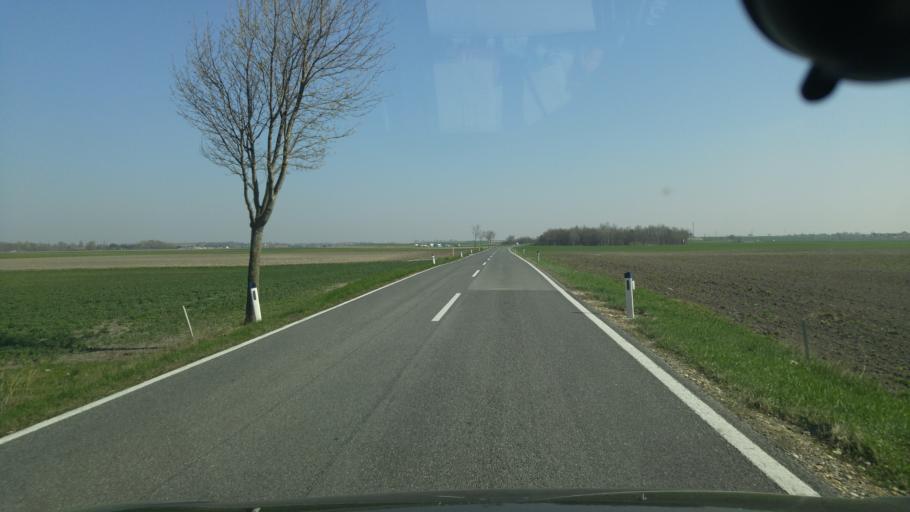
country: AT
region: Lower Austria
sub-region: Politischer Bezirk Wien-Umgebung
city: Moosbrunn
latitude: 48.0101
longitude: 16.4279
